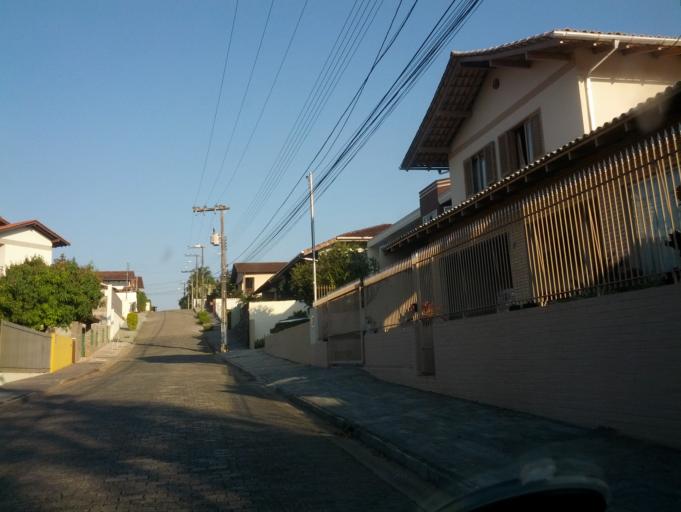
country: BR
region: Santa Catarina
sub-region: Blumenau
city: Blumenau
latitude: -26.9083
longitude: -49.0861
